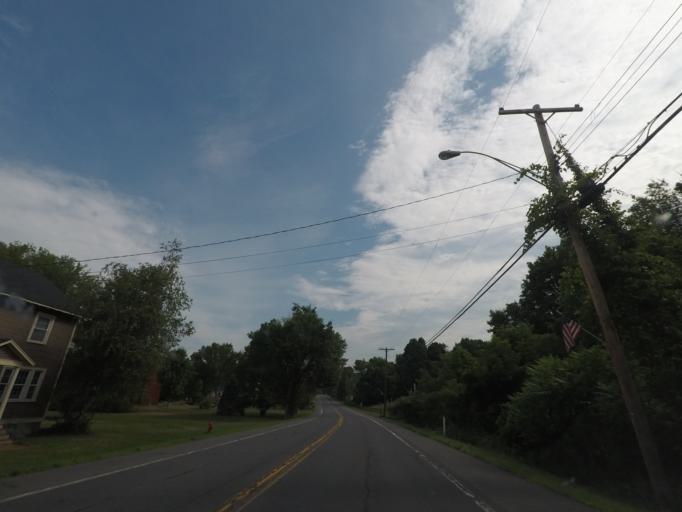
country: US
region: New York
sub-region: Rensselaer County
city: Poestenkill
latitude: 42.6928
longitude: -73.5618
